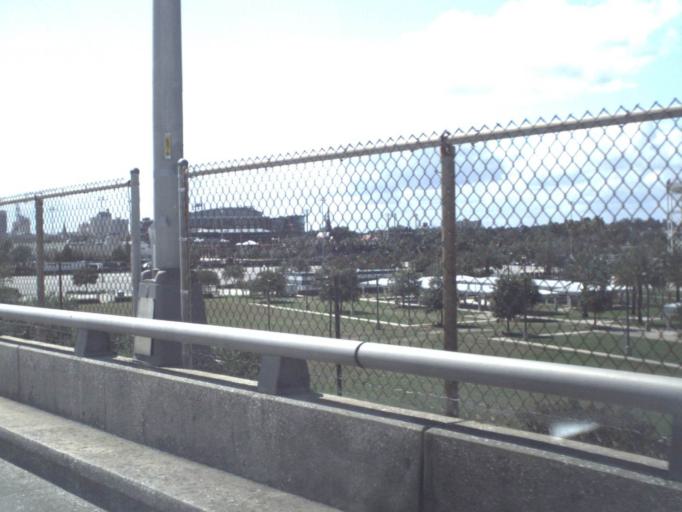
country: US
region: Florida
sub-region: Duval County
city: Jacksonville
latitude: 30.3210
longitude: -81.6372
